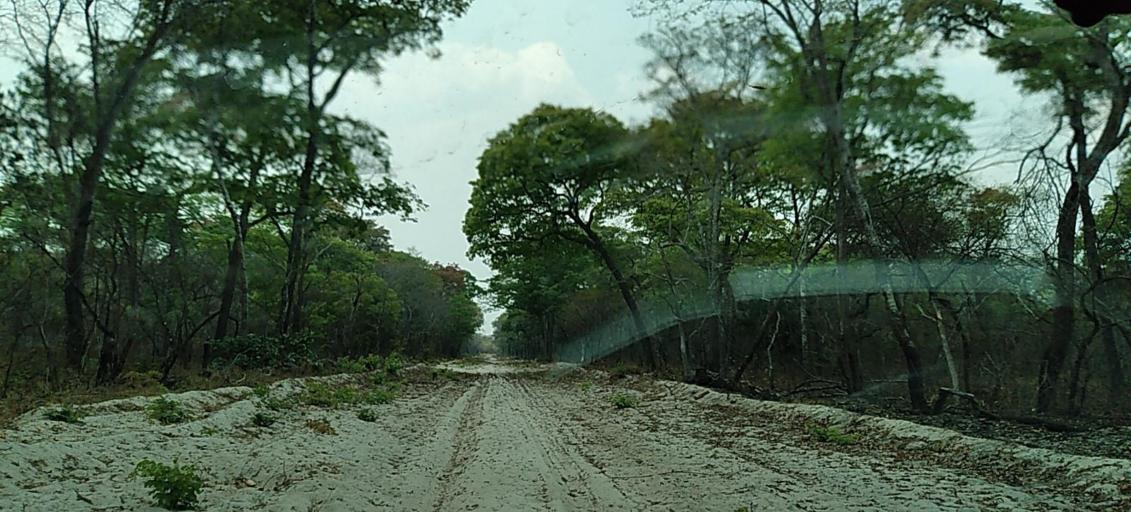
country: ZM
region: Western
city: Lukulu
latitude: -14.0109
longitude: 23.5819
